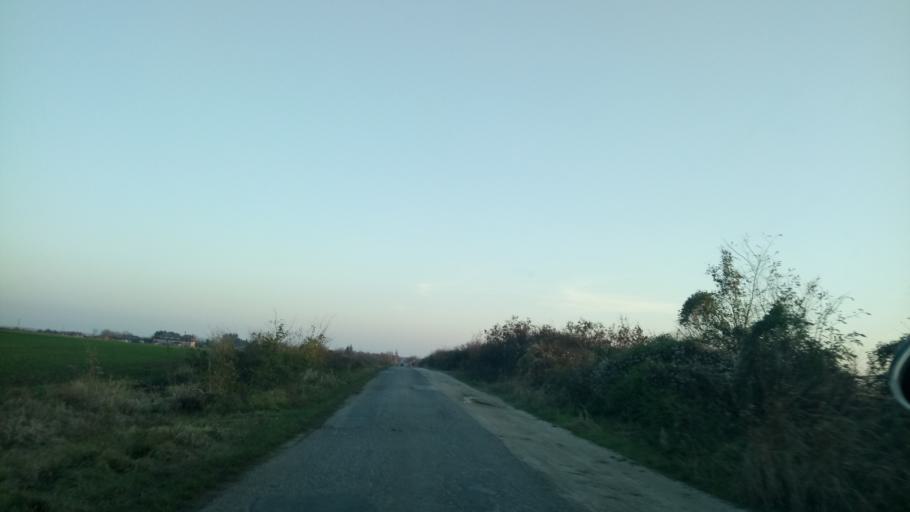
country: RS
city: Surduk
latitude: 45.1031
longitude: 20.2863
